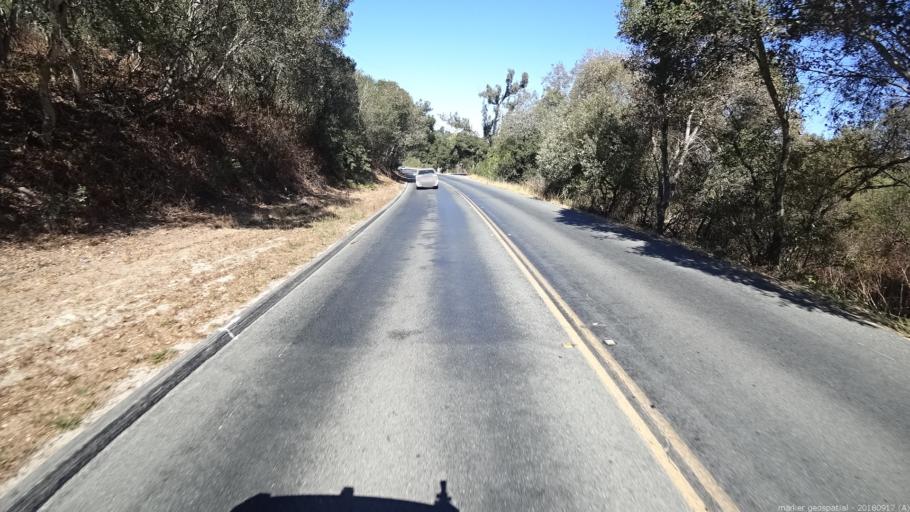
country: US
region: California
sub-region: Monterey County
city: Prunedale
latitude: 36.8144
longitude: -121.6257
